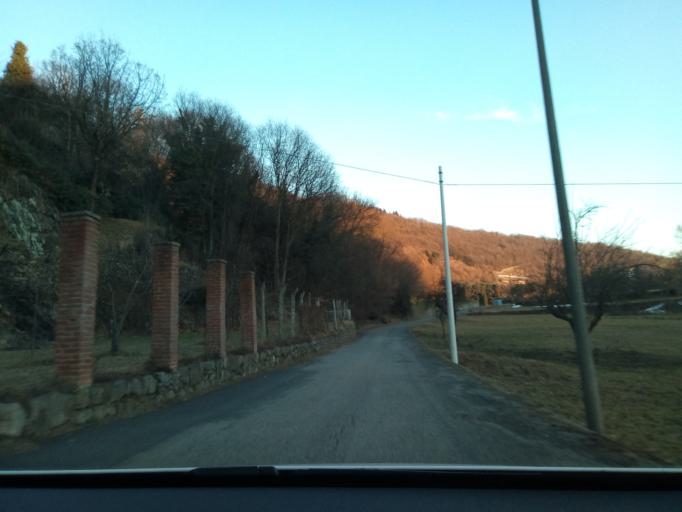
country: IT
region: Piedmont
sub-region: Provincia di Torino
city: Chiaverano
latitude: 45.4973
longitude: 7.9126
